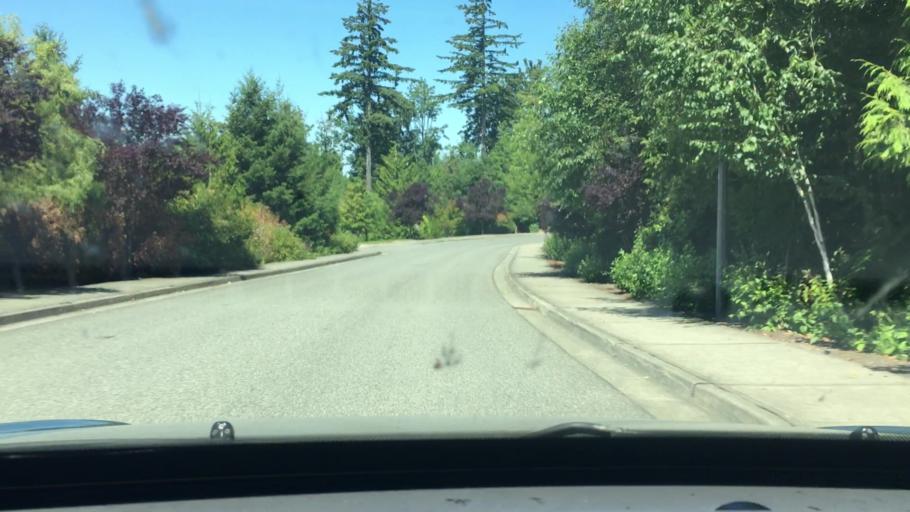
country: US
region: Washington
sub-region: King County
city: Newcastle
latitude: 47.5400
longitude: -122.1191
